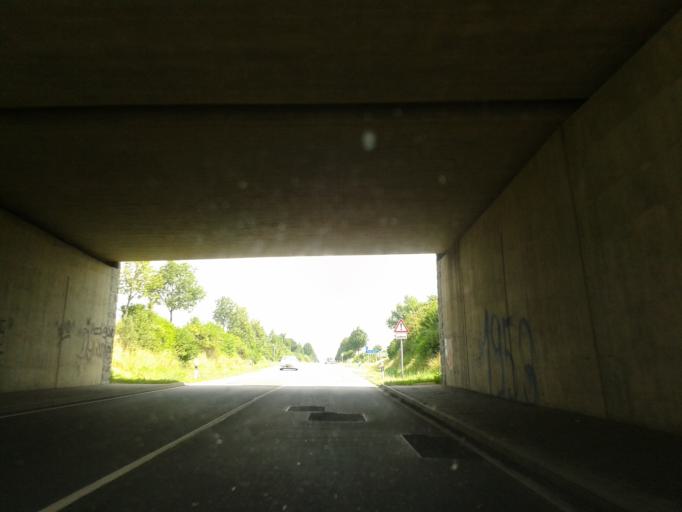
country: DE
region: Saxony
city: Goda
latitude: 51.1919
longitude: 14.3613
